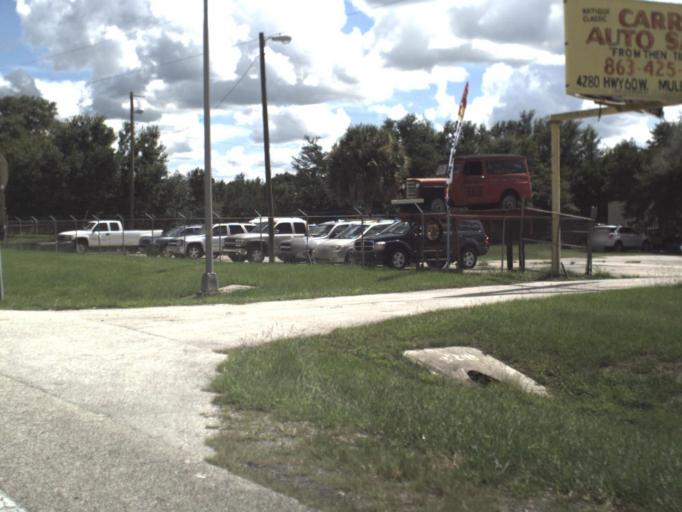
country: US
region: Florida
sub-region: Polk County
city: Willow Oak
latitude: 27.9194
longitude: -82.0259
